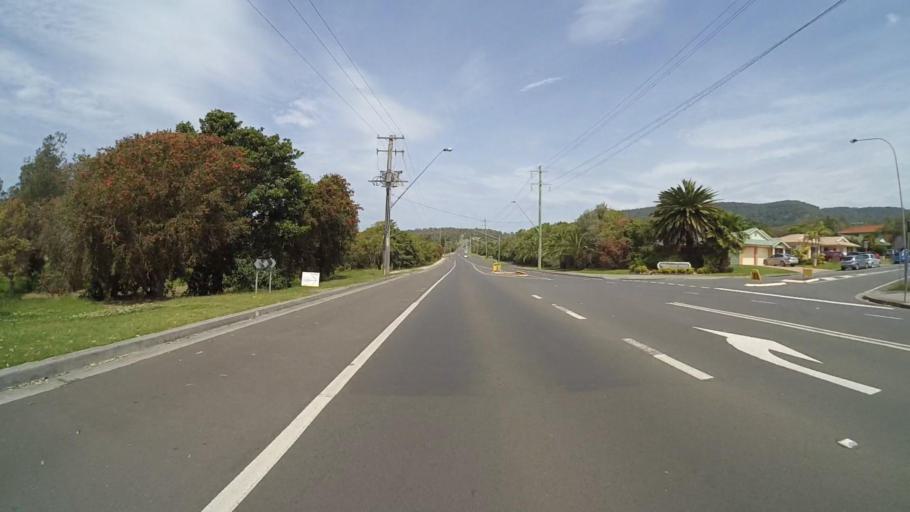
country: AU
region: New South Wales
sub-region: Shellharbour
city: Albion Park Rail
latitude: -34.5837
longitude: 150.7787
